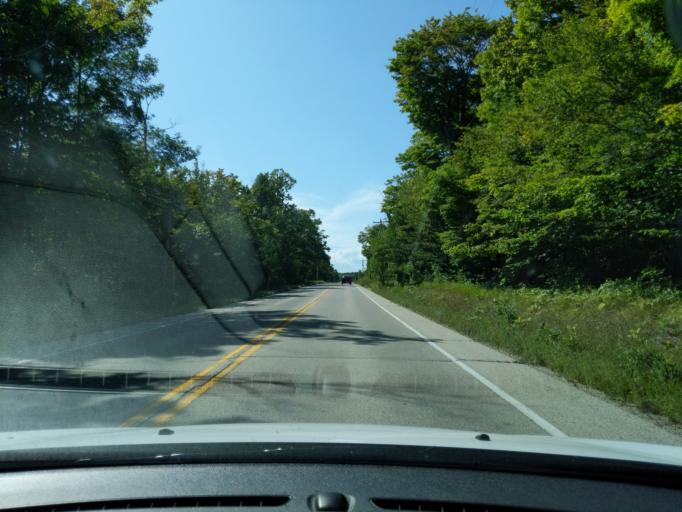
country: US
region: Michigan
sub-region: Delta County
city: Escanaba
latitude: 45.2594
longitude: -87.0370
